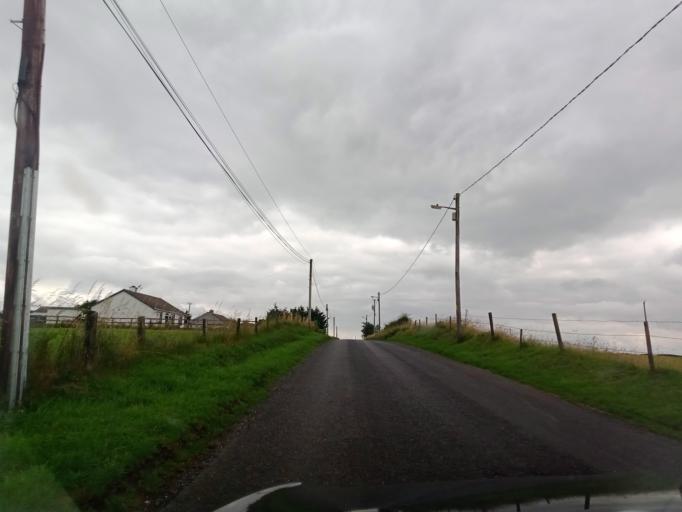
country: IE
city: Ballylinan
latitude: 52.8966
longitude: -7.1305
